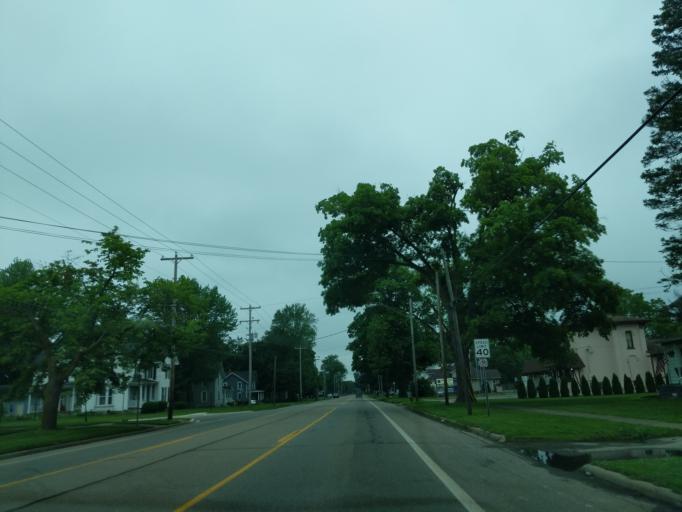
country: US
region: Michigan
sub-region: Branch County
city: Quincy
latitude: 41.9462
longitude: -84.8765
